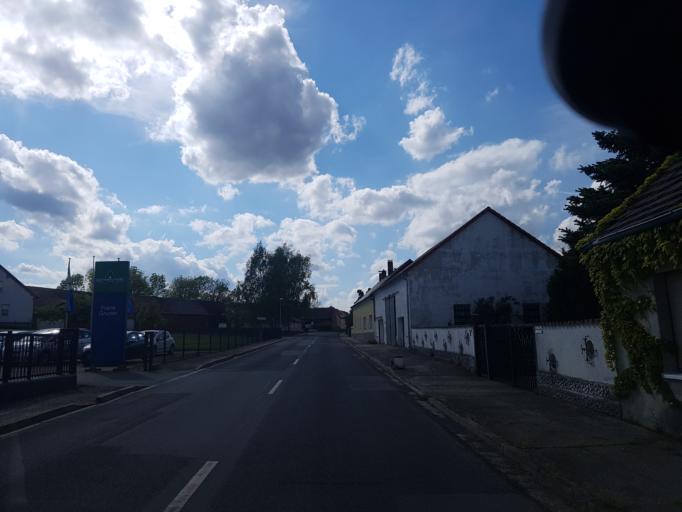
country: DE
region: Brandenburg
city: Cottbus
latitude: 51.6776
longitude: 14.3635
